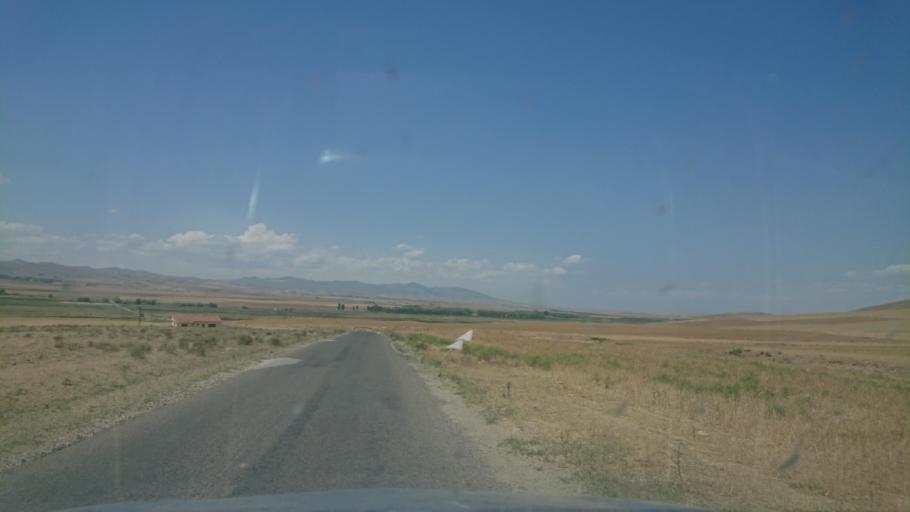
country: TR
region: Aksaray
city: Sariyahsi
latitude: 39.0057
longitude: 33.9137
